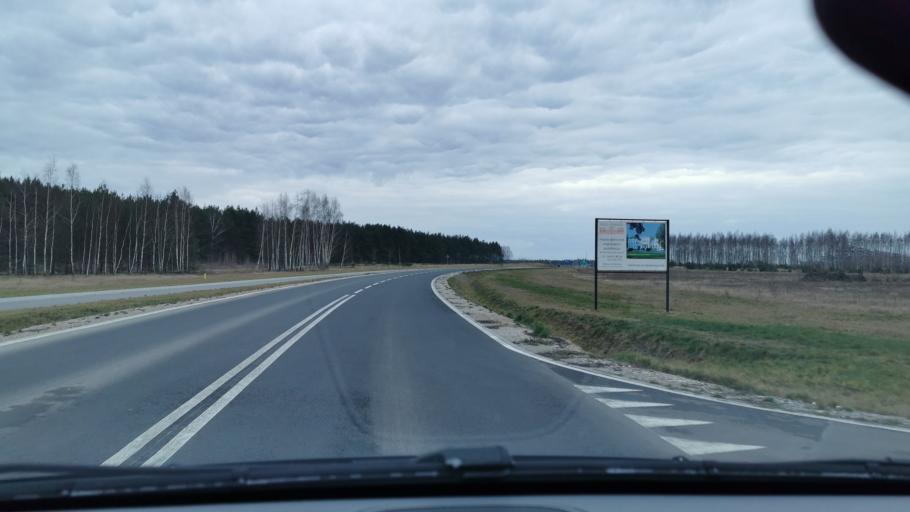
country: PL
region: Masovian Voivodeship
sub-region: Powiat zyrardowski
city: Zyrardow
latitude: 51.9954
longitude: 20.4646
